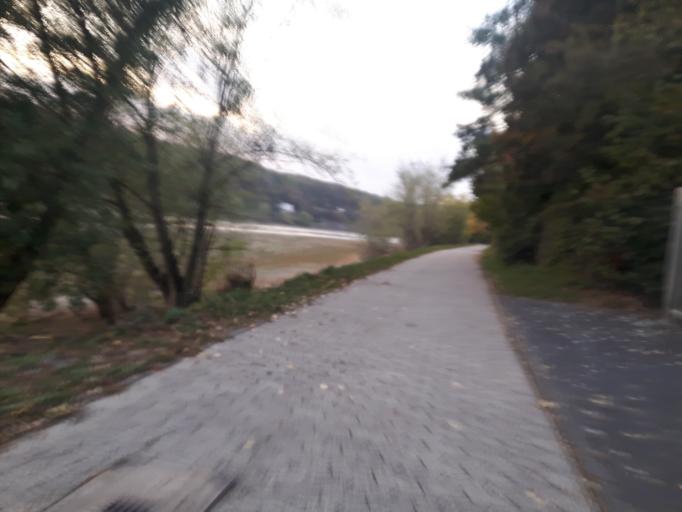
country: DE
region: Rheinland-Pfalz
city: Remagen
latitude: 50.5843
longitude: 7.2277
